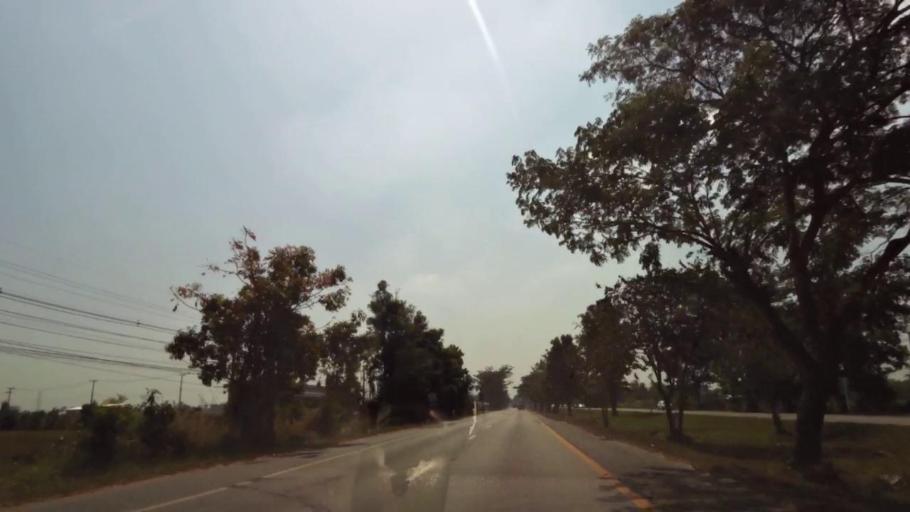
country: TH
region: Phichit
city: Wachira Barami
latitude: 16.5401
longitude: 100.1448
